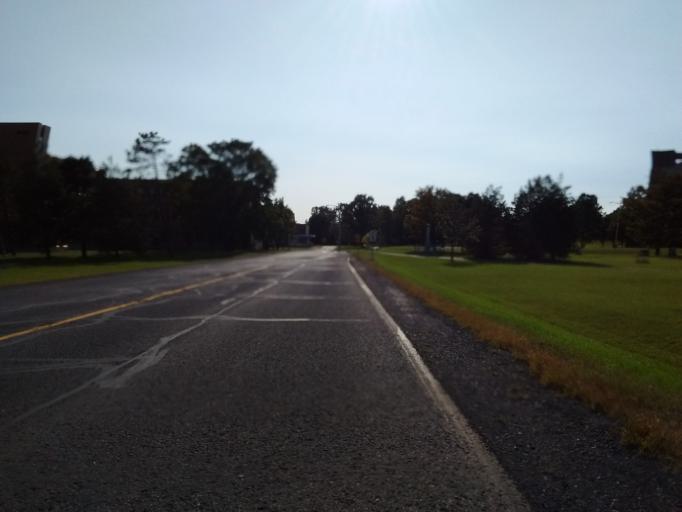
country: CA
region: Ontario
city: Ottawa
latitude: 45.4434
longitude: -75.6158
